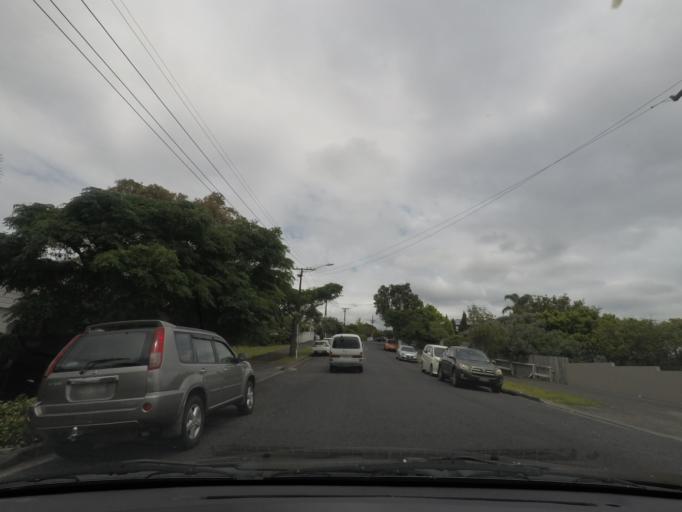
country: NZ
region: Auckland
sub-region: Auckland
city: Auckland
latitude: -36.8679
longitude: 174.7837
